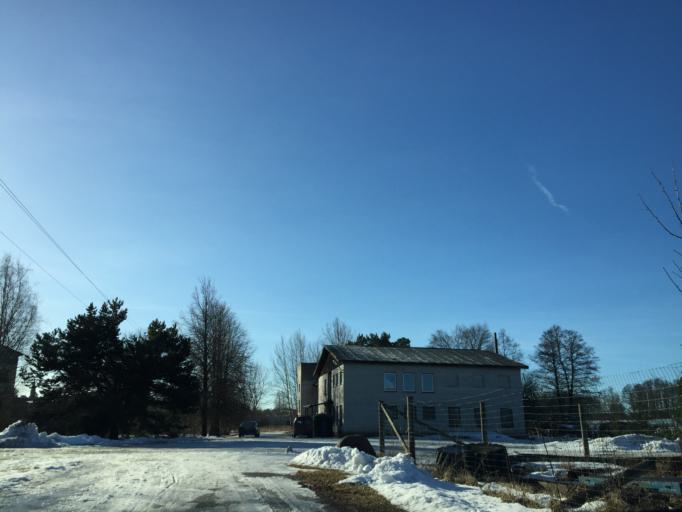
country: LV
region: Salacgrivas
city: Ainazi
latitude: 58.0832
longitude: 24.4987
